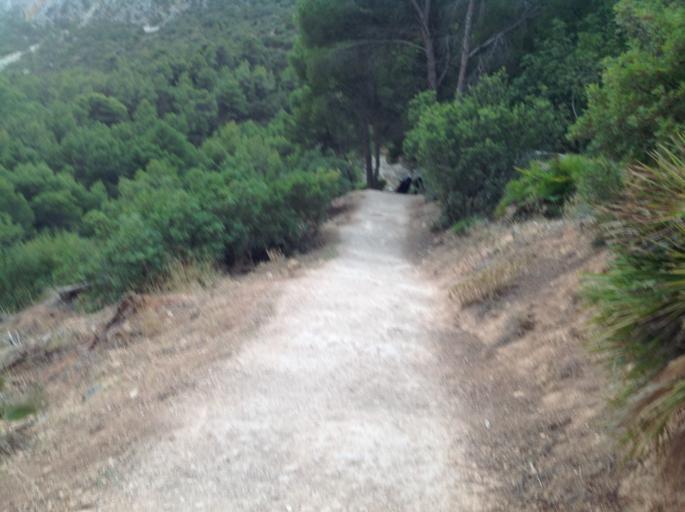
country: ES
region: Andalusia
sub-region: Provincia de Malaga
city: Ardales
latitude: 36.9253
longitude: -4.7827
